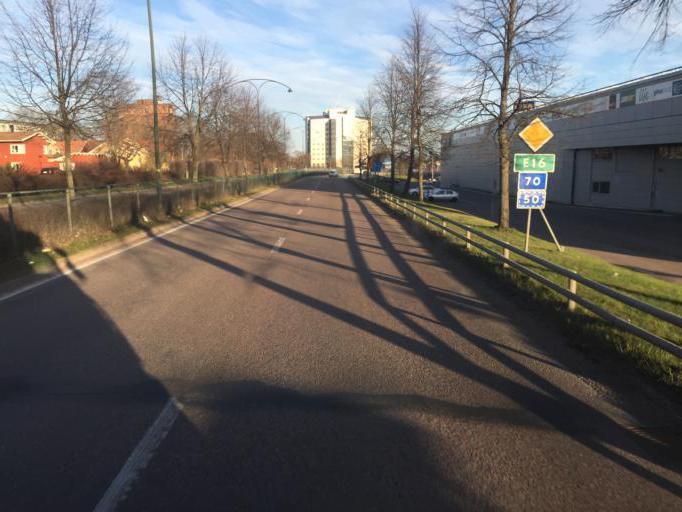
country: SE
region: Dalarna
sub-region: Borlange Kommun
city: Borlaenge
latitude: 60.4858
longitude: 15.4183
